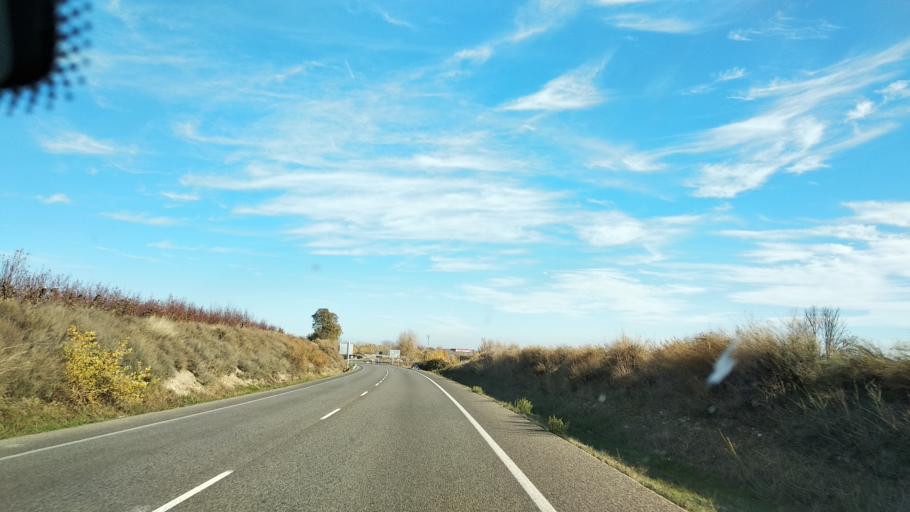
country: ES
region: Catalonia
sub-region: Provincia de Lleida
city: Corbins
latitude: 41.6823
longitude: 0.6908
